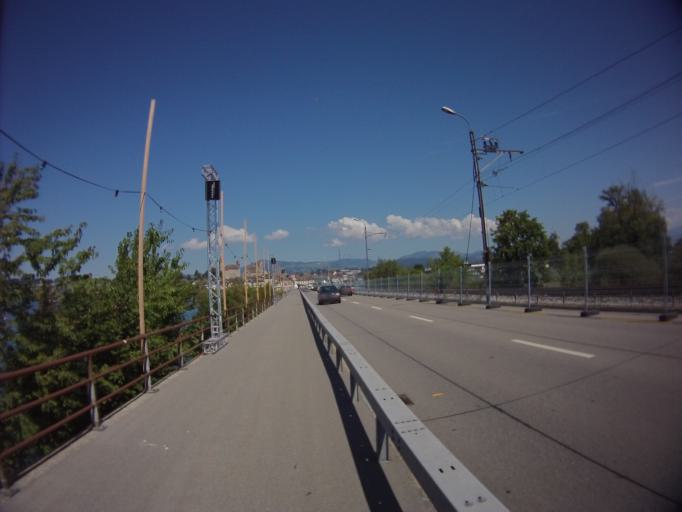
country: CH
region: Saint Gallen
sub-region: Wahlkreis See-Gaster
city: Rapperswil
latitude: 47.2216
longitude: 8.8108
